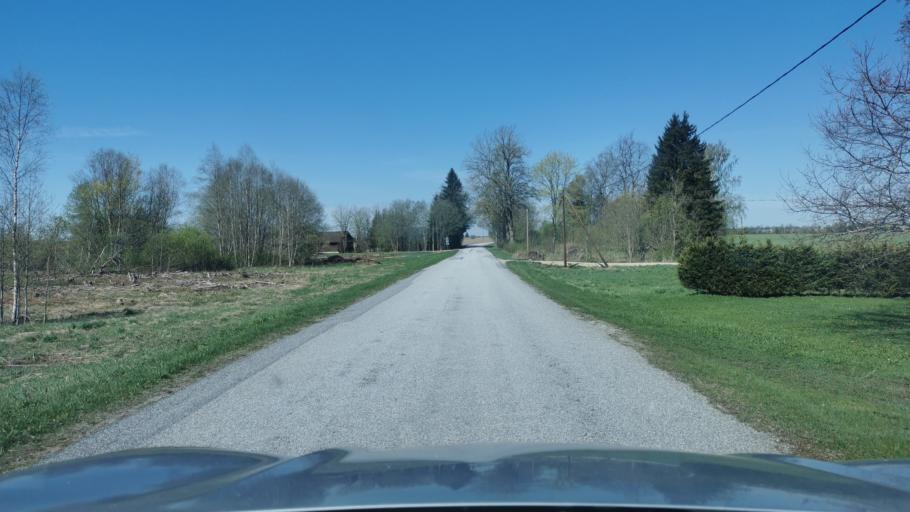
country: EE
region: Laeaene-Virumaa
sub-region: Vinni vald
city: Vinni
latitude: 59.0482
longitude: 26.6095
